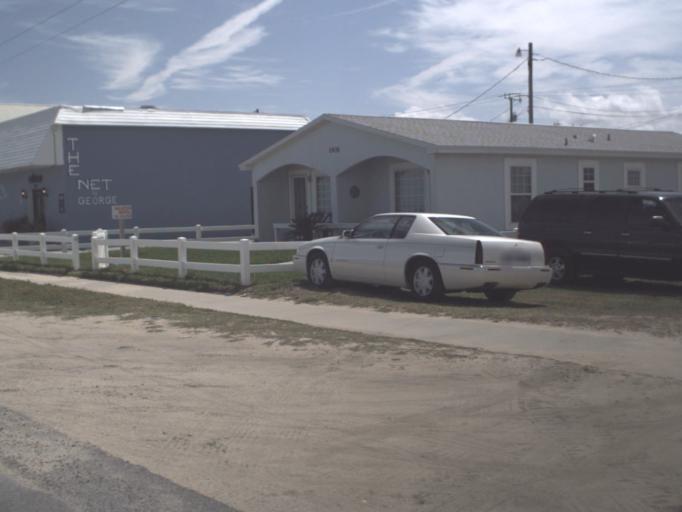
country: US
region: Florida
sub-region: Flagler County
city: Flagler Beach
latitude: 29.4615
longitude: -81.1181
